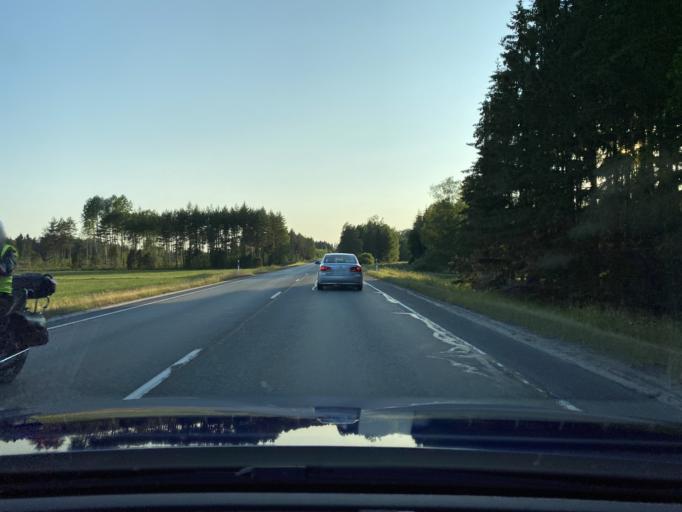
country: FI
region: Haeme
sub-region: Forssa
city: Tammela
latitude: 60.8261
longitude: 23.7570
